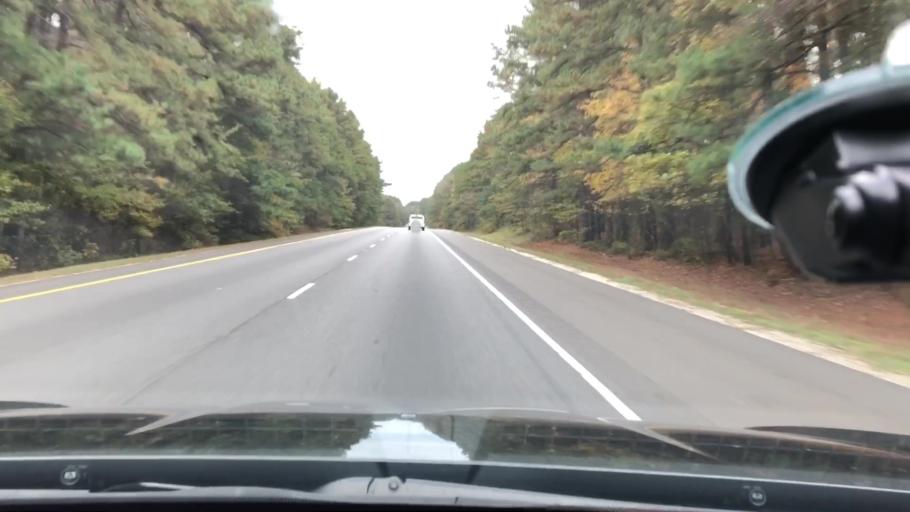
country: US
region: Arkansas
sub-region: Hot Spring County
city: Malvern
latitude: 34.3019
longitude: -92.9444
